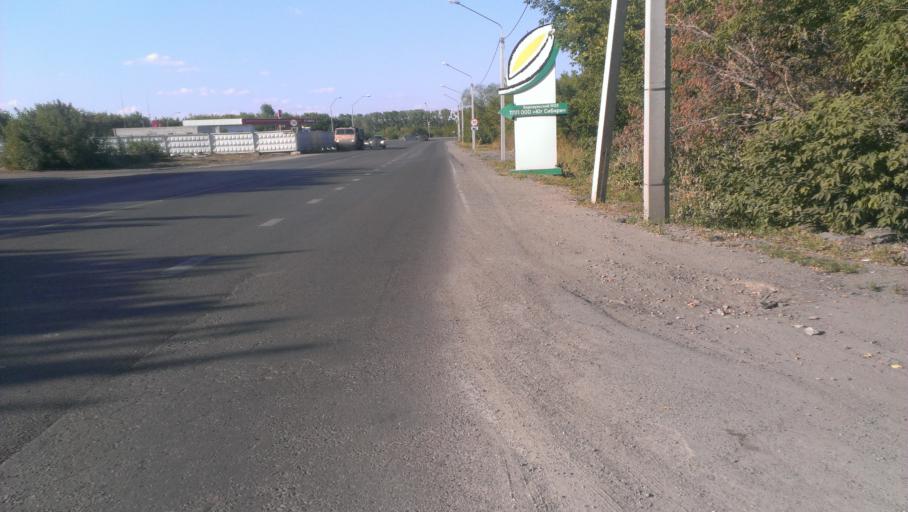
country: RU
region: Altai Krai
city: Novosilikatnyy
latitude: 53.3474
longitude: 83.6202
